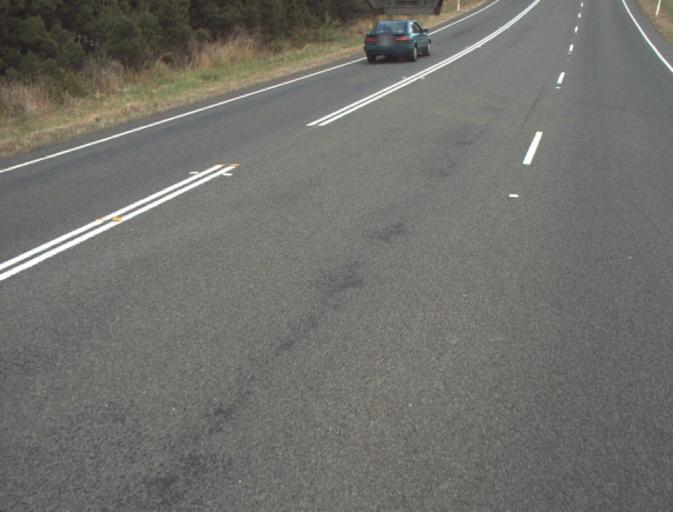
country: AU
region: Tasmania
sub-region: Launceston
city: Mayfield
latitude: -41.2815
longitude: 147.0388
